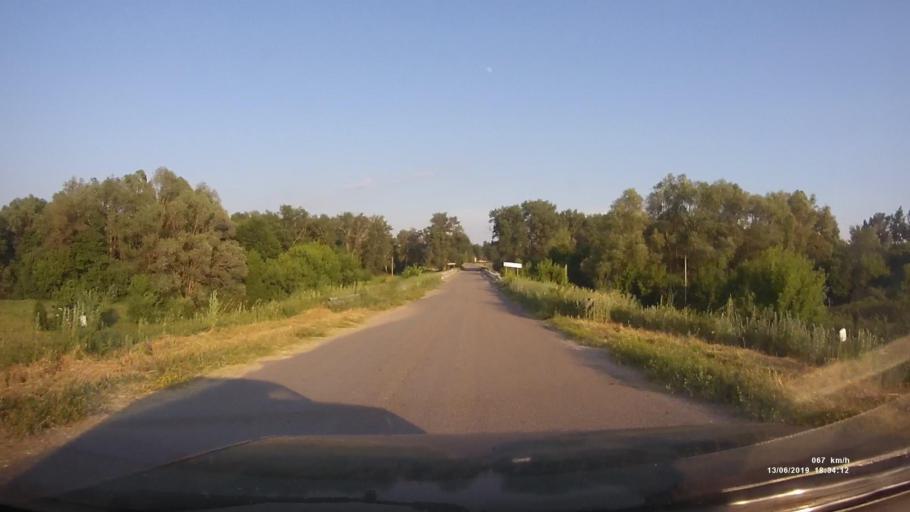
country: RU
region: Rostov
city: Kazanskaya
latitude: 49.8692
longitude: 41.3936
